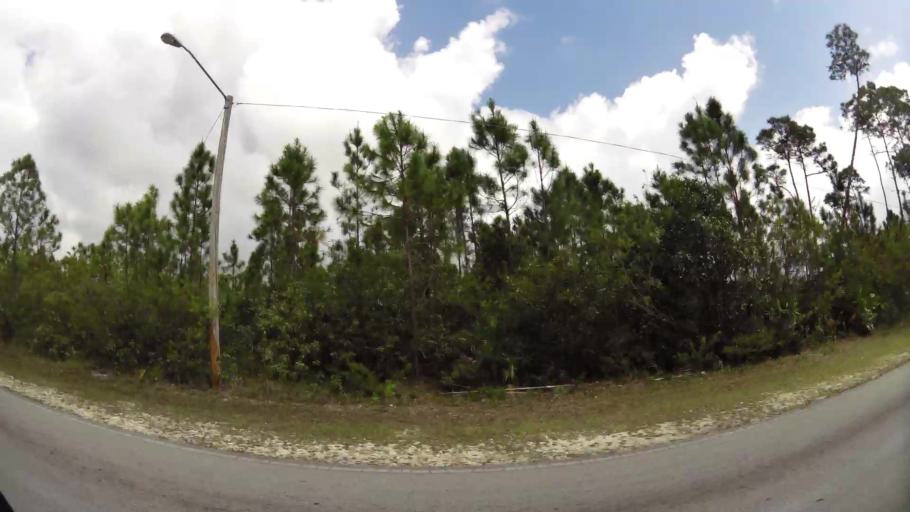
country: BS
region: Freeport
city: Lucaya
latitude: 26.5372
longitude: -78.6454
